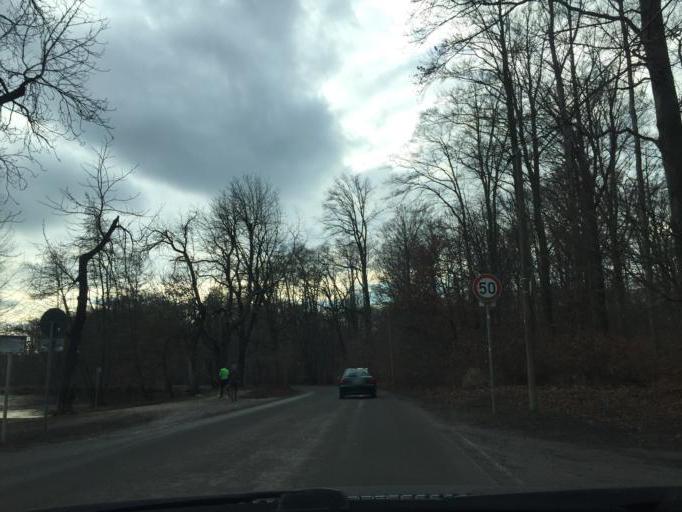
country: DE
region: Saxony
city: Moritzburg
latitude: 51.1695
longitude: 13.6731
